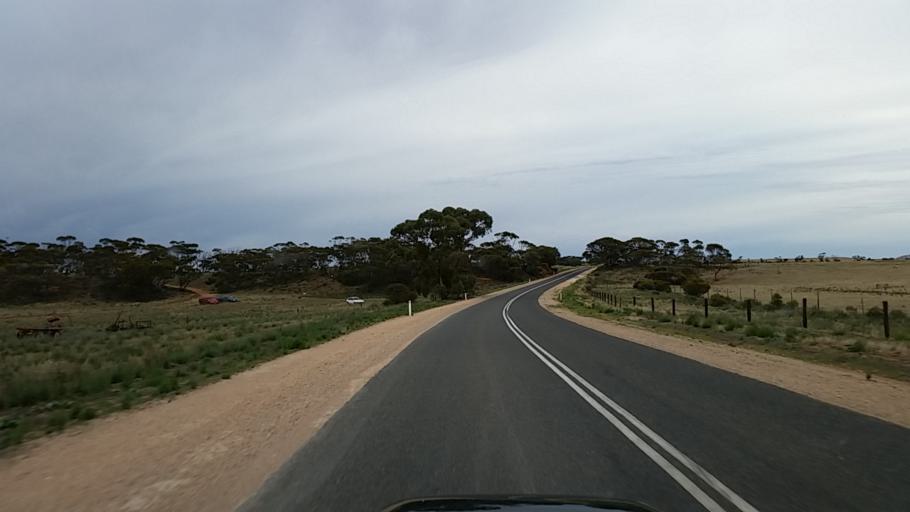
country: AU
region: South Australia
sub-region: Mid Murray
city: Mannum
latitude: -34.7552
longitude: 139.3061
